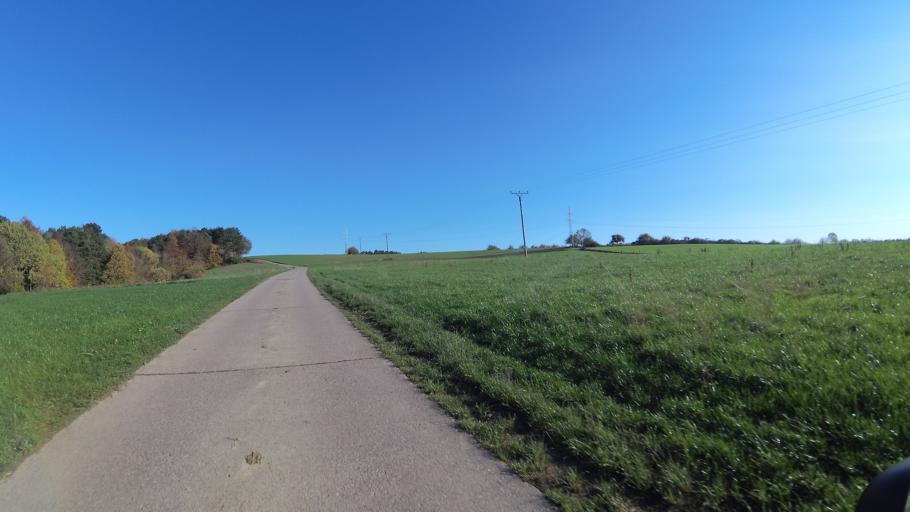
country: DE
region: Saarland
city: Losheim
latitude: 49.4735
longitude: 6.7350
